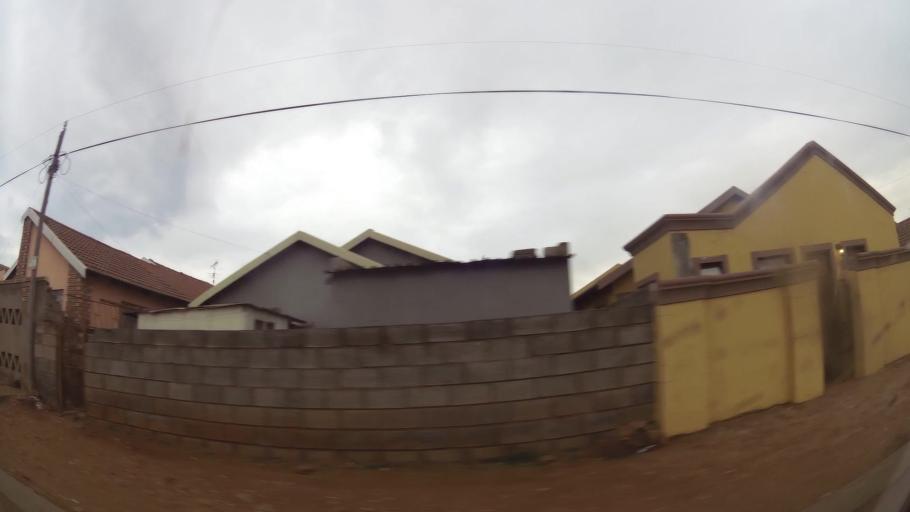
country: ZA
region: Gauteng
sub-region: Ekurhuleni Metropolitan Municipality
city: Germiston
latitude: -26.3710
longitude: 28.1661
